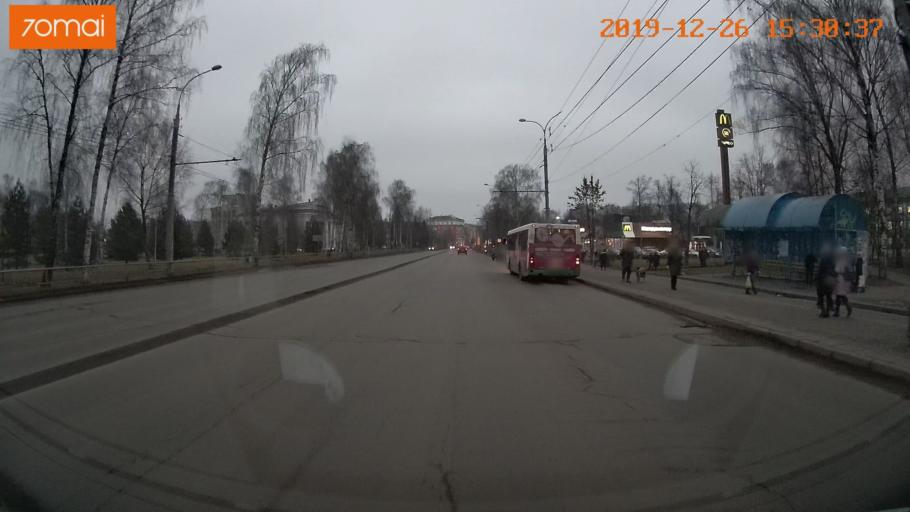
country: RU
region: Jaroslavl
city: Rybinsk
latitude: 58.0550
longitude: 38.8166
